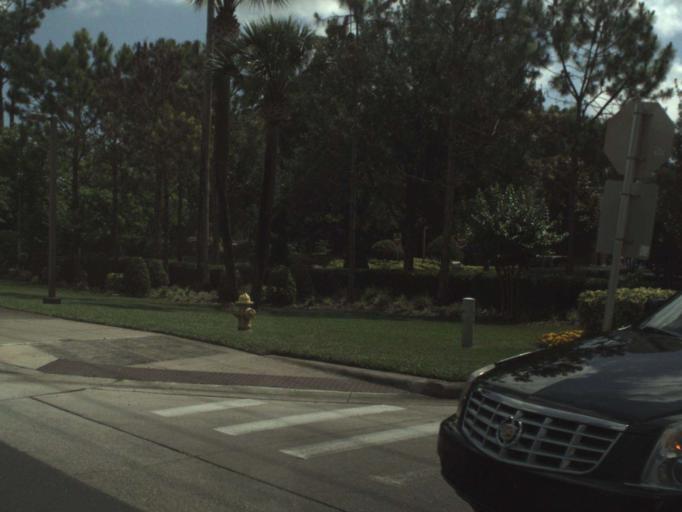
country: US
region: Florida
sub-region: Volusia County
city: Port Orange
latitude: 29.1096
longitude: -81.0261
